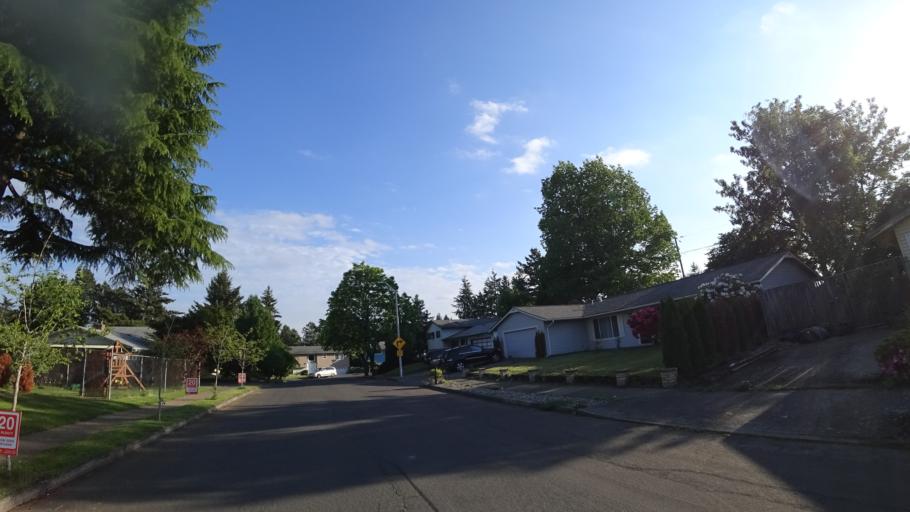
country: US
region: Oregon
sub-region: Multnomah County
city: Gresham
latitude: 45.5094
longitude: -122.4987
